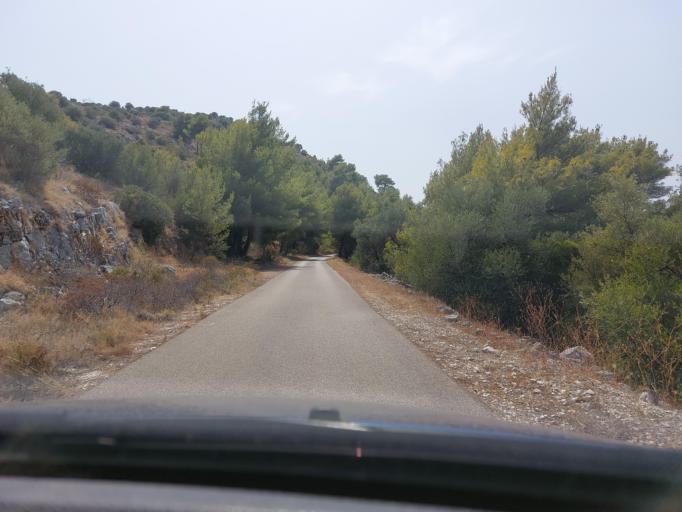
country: HR
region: Dubrovacko-Neretvanska
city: Smokvica
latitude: 42.7299
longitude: 16.8905
